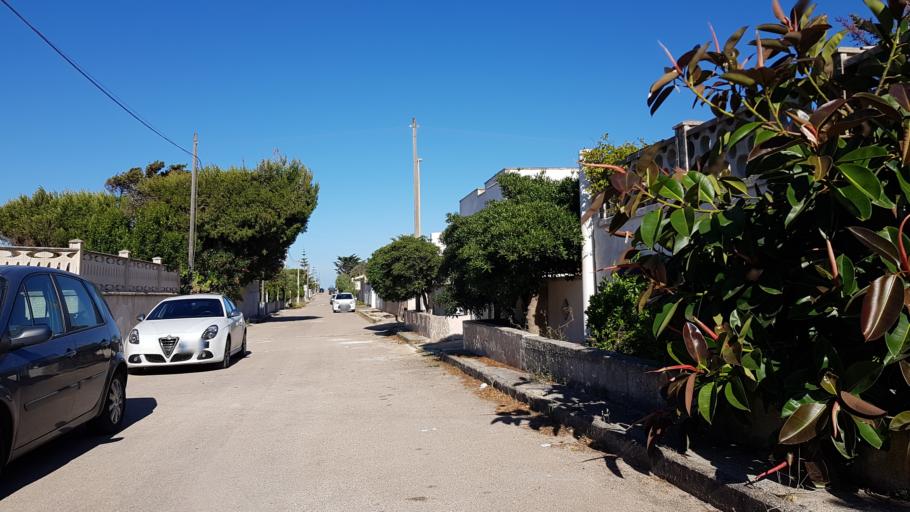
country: IT
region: Apulia
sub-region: Provincia di Brindisi
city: Brindisi
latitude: 40.6841
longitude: 17.8702
